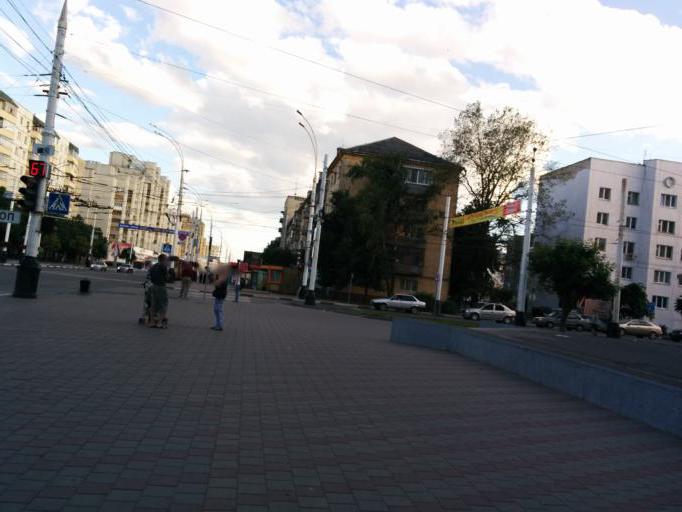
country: RU
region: Tambov
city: Tambov
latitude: 52.7380
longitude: 41.4517
